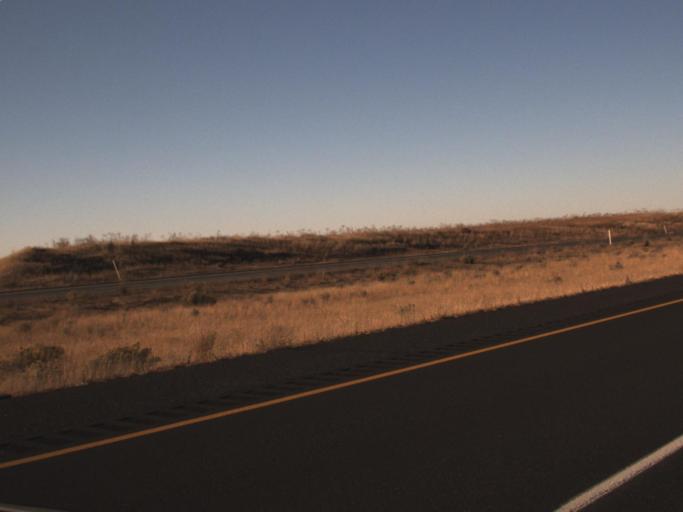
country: US
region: Washington
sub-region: Franklin County
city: Connell
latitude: 46.6013
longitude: -118.9295
